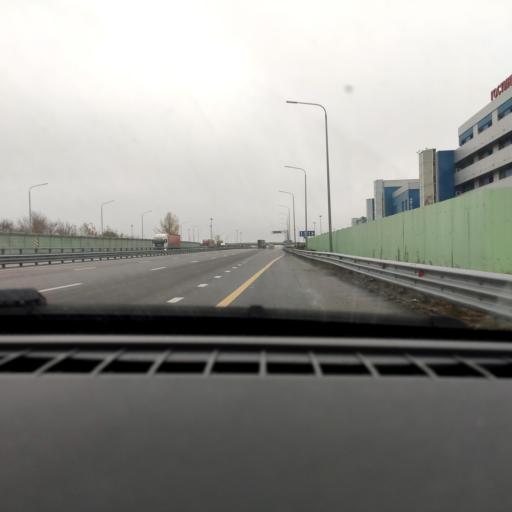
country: RU
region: Voronezj
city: Somovo
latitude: 51.6825
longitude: 39.3017
